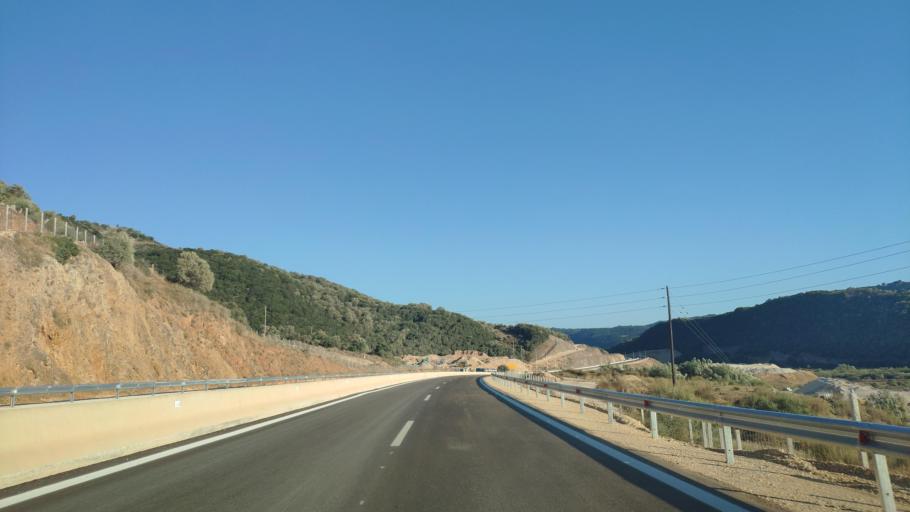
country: GR
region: West Greece
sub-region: Nomos Aitolias kai Akarnanias
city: Katouna
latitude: 38.7938
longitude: 21.1399
